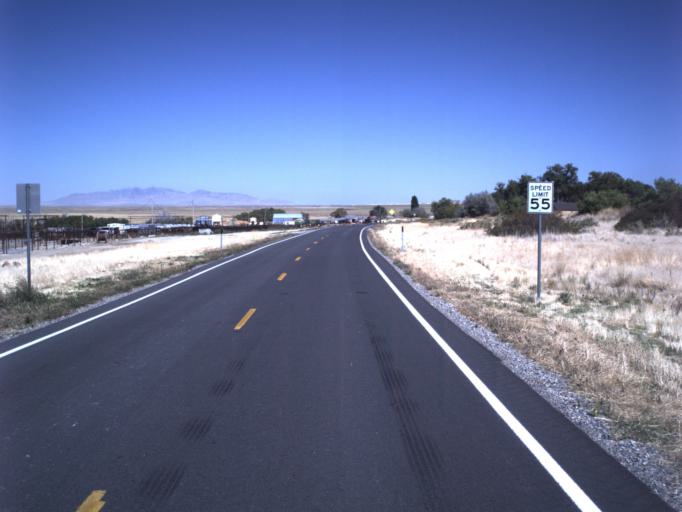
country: US
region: Utah
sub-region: Tooele County
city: Grantsville
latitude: 40.5334
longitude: -112.7476
